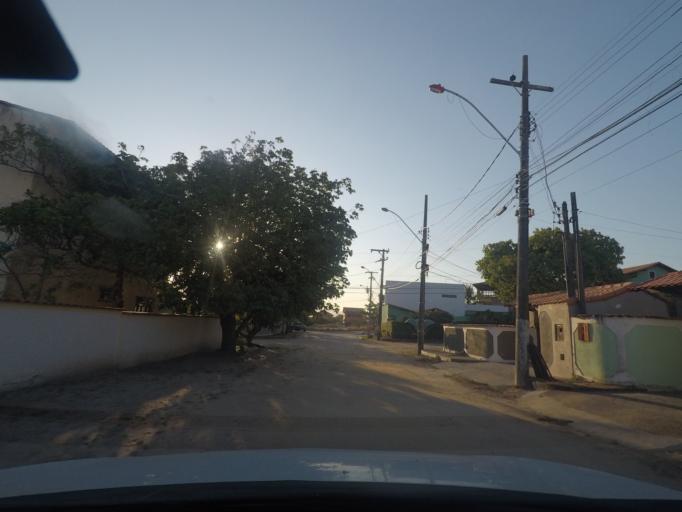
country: BR
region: Rio de Janeiro
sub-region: Marica
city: Marica
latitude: -22.9696
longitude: -42.9312
